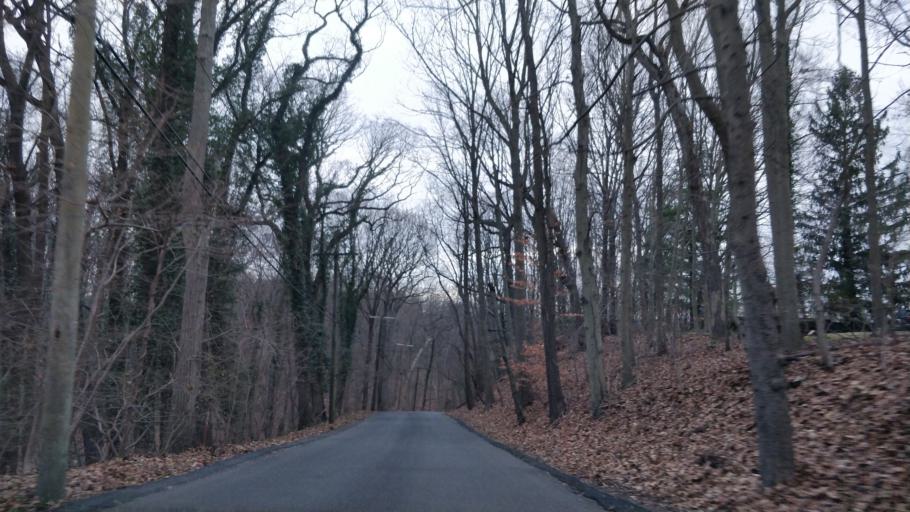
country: US
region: New York
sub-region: Nassau County
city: Oyster Bay Cove
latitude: 40.8801
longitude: -73.4994
